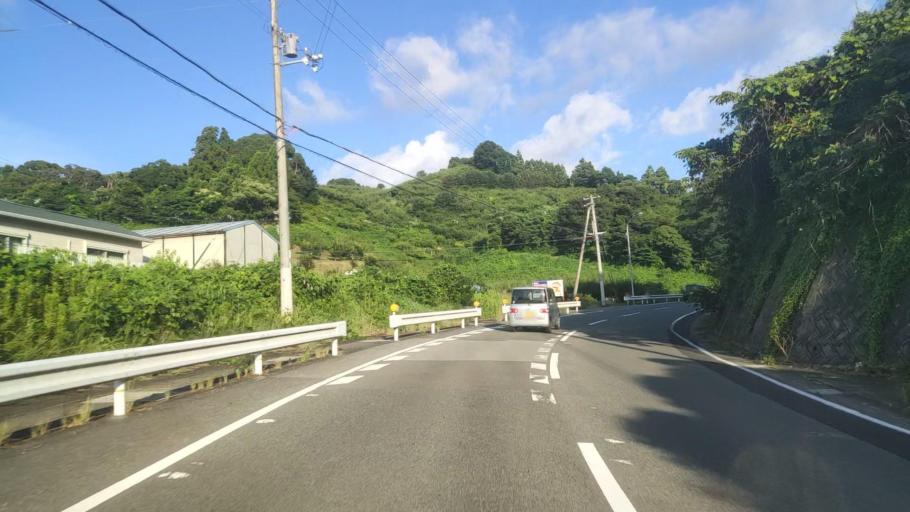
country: JP
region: Wakayama
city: Tanabe
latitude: 33.7339
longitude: 135.4322
